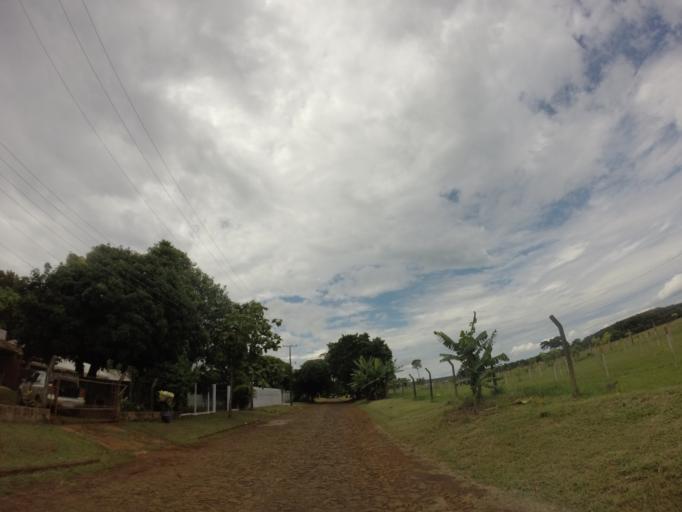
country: PY
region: Alto Parana
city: Ciudad del Este
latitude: -25.4067
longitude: -54.6217
